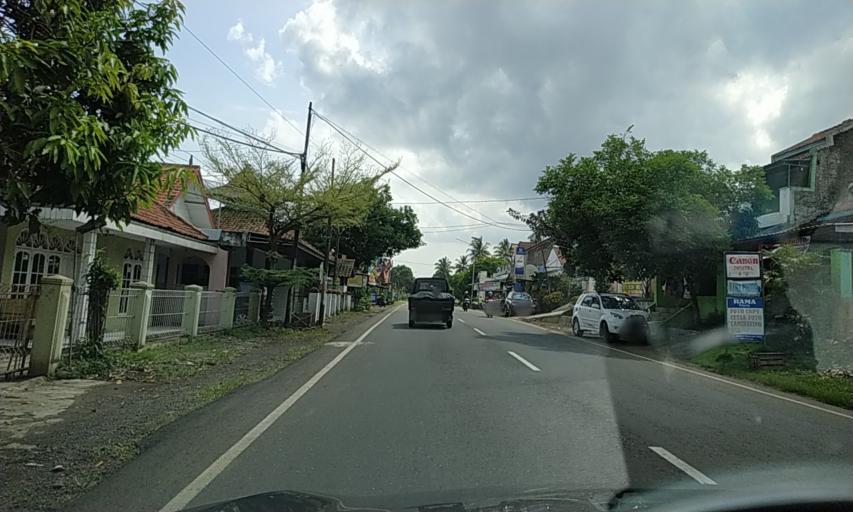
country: ID
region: Central Java
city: Cihandiwung Lor
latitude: -7.3354
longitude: 108.6914
